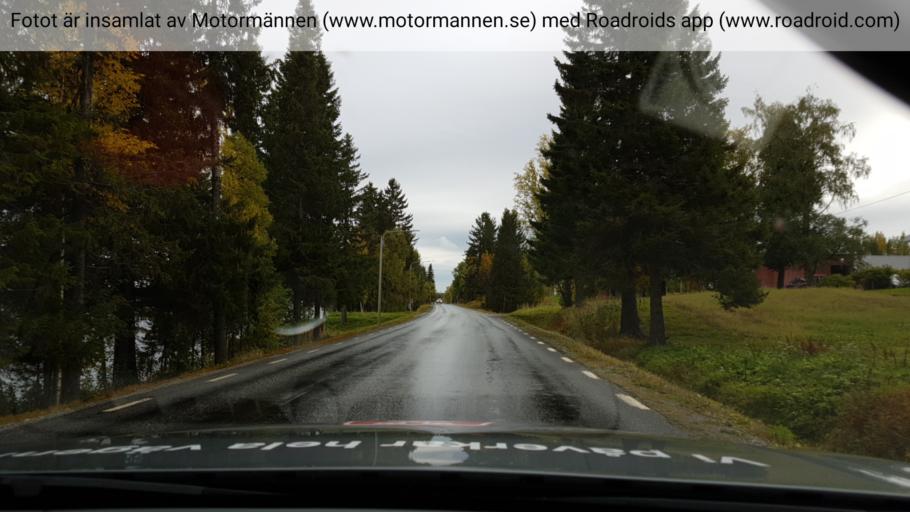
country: SE
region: Vaesterbotten
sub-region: Vilhelmina Kommun
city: Sjoberg
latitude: 64.6677
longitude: 16.3015
